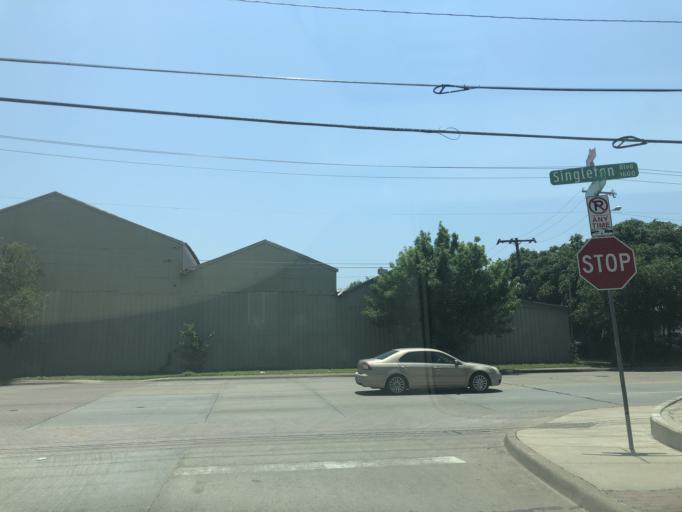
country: US
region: Texas
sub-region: Dallas County
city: Dallas
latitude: 32.7788
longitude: -96.8457
